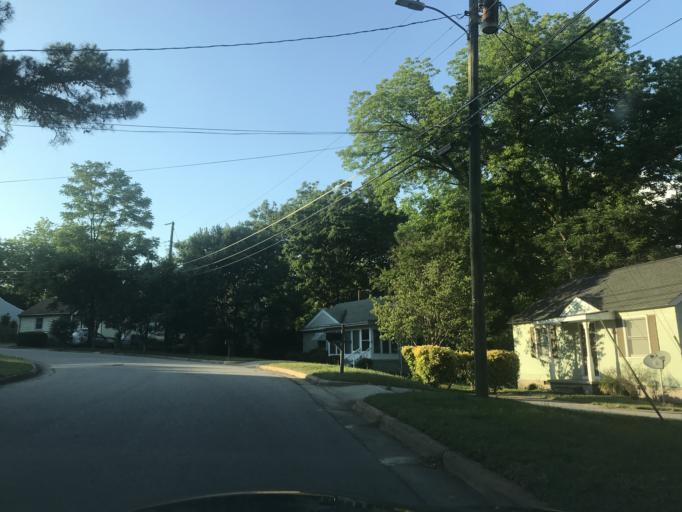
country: US
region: North Carolina
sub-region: Wake County
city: Raleigh
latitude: 35.7473
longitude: -78.6423
